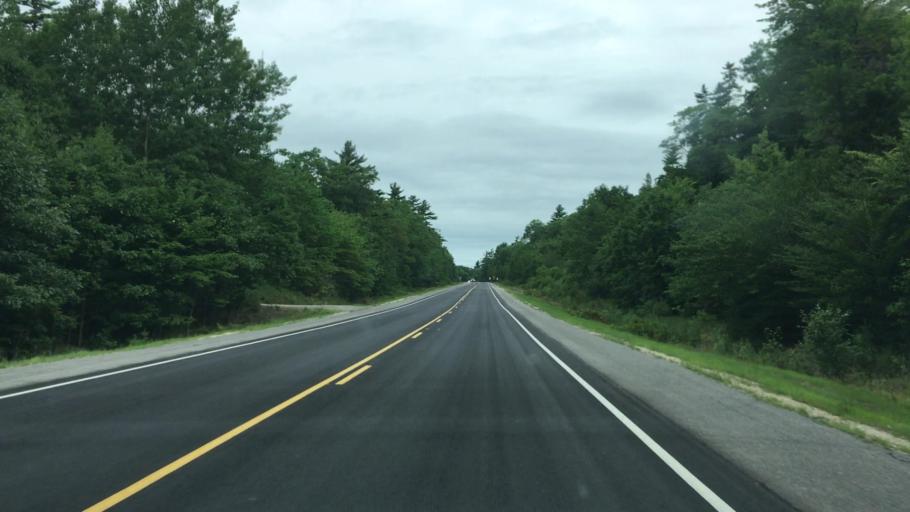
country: US
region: Maine
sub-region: Washington County
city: Cherryfield
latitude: 44.9001
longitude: -67.8558
